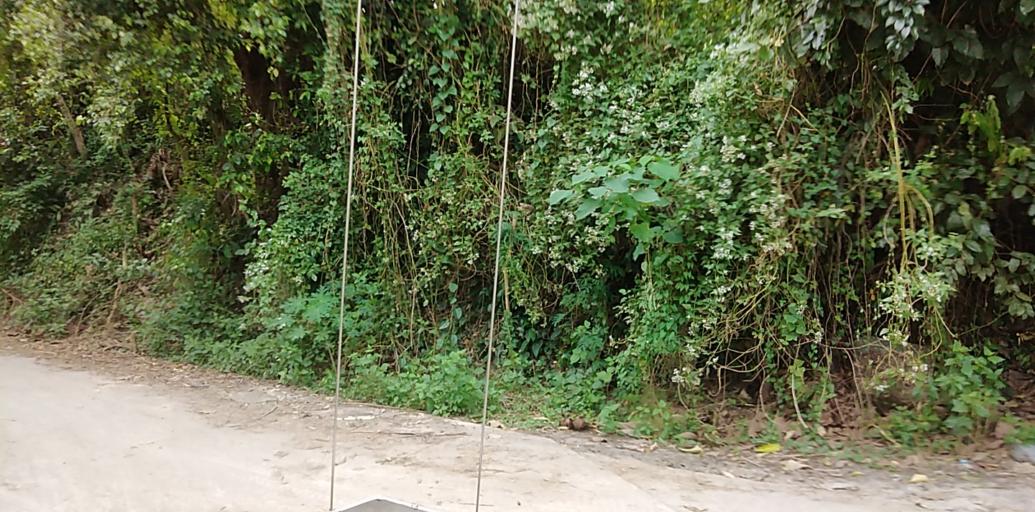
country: PH
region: Central Luzon
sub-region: Province of Pampanga
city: Porac
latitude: 15.0574
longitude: 120.5330
